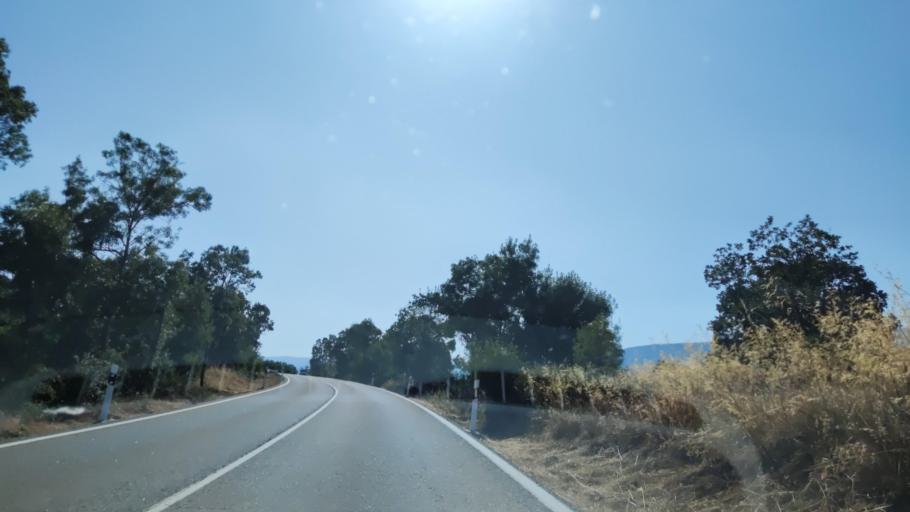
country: ES
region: Madrid
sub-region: Provincia de Madrid
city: Lozoya
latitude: 40.9495
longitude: -3.7711
